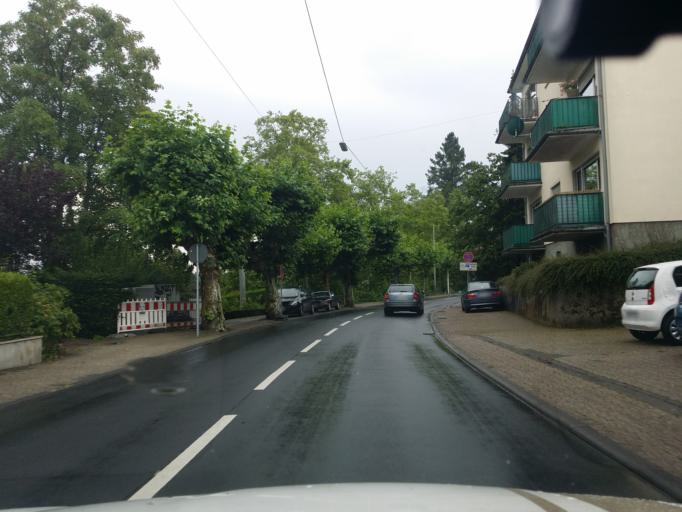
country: DE
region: Hesse
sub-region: Regierungsbezirk Darmstadt
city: Kronberg
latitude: 50.1828
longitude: 8.5092
